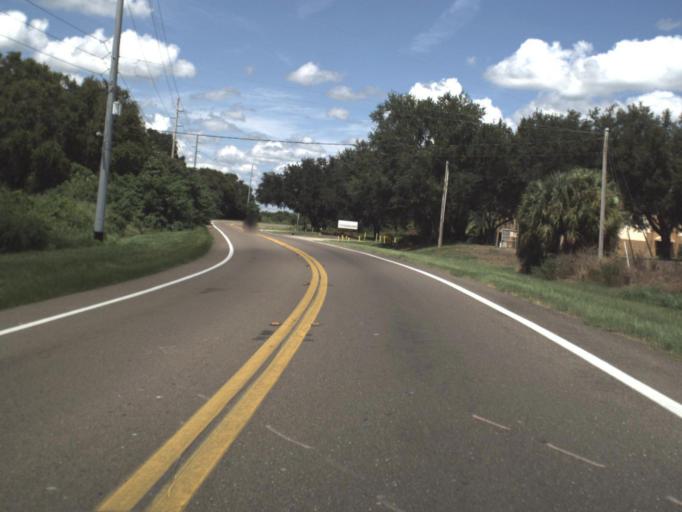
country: US
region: Florida
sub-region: Polk County
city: Winter Haven
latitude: 28.0528
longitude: -81.7212
